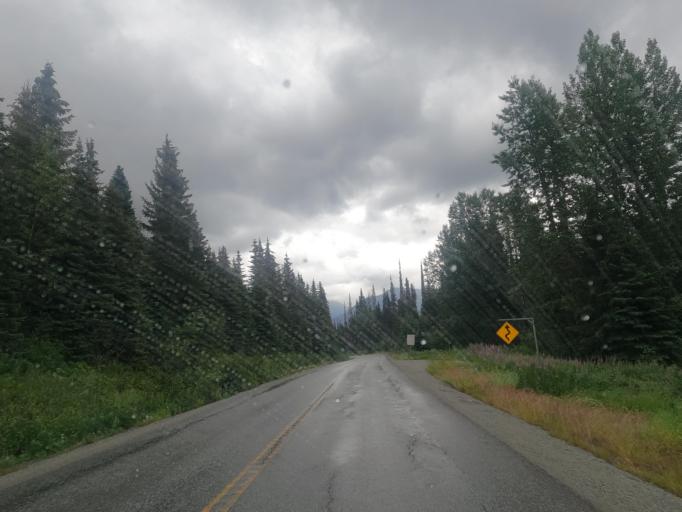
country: CA
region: British Columbia
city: Pemberton
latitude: 50.3869
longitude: -122.4576
